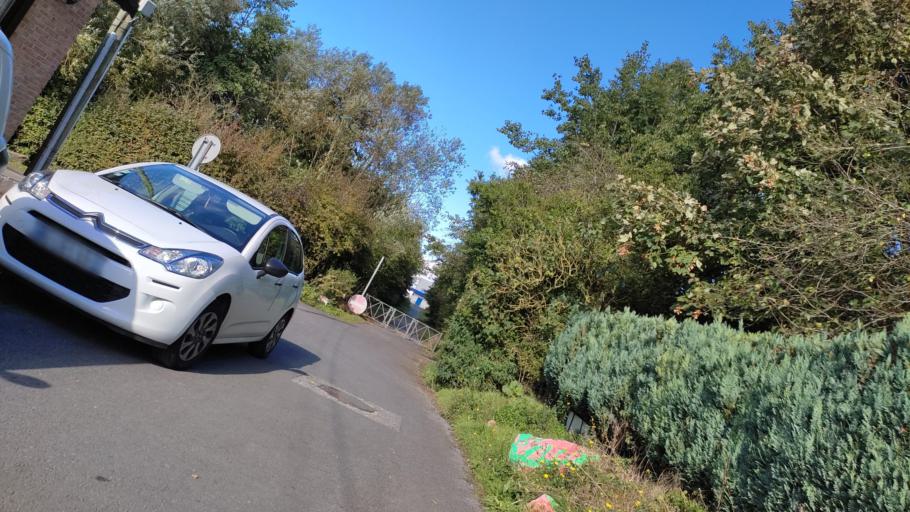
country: FR
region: Nord-Pas-de-Calais
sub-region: Departement du Pas-de-Calais
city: Saint-Laurent-Blangy
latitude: 50.3114
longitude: 2.8228
